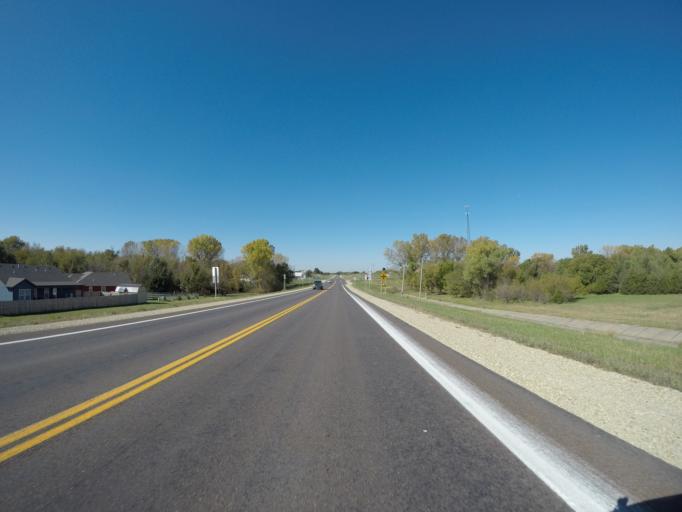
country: US
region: Kansas
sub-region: Riley County
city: Fort Riley North
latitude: 39.3036
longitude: -96.8278
